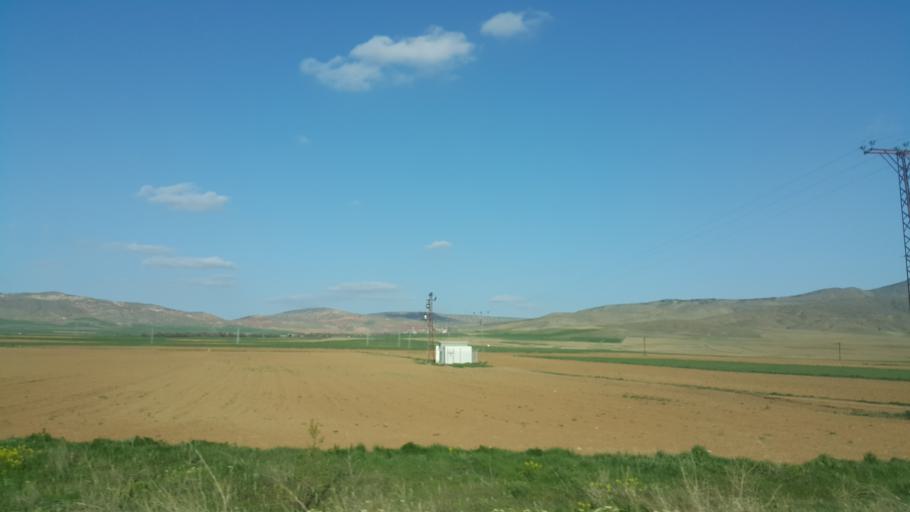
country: TR
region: Ankara
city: Sereflikochisar
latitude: 38.8545
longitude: 33.5896
